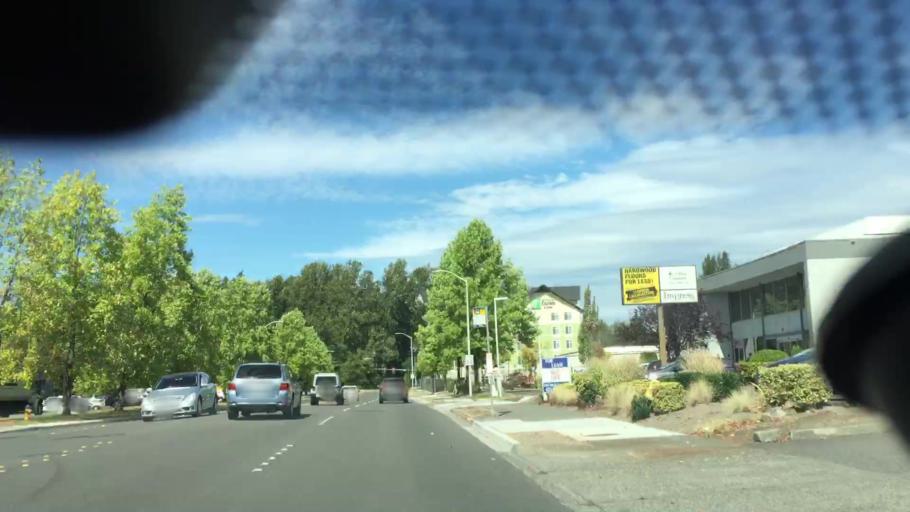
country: US
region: Washington
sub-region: King County
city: Tukwila
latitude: 47.4592
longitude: -122.2499
